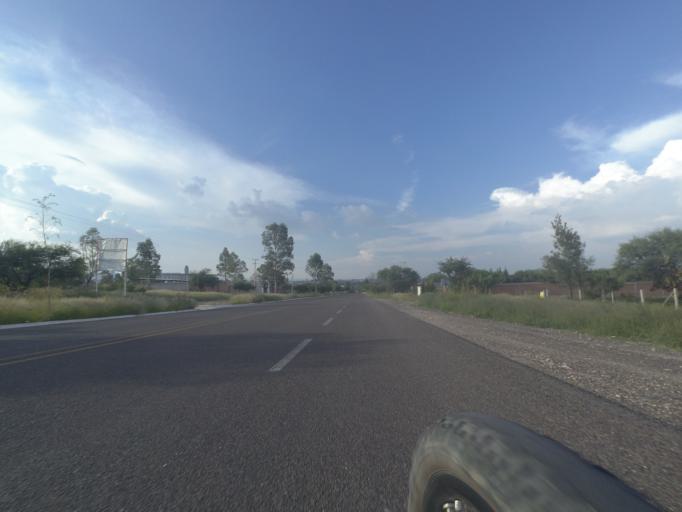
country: MX
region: Aguascalientes
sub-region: Aguascalientes
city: Penuelas (El Cienegal)
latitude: 21.7499
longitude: -102.3506
